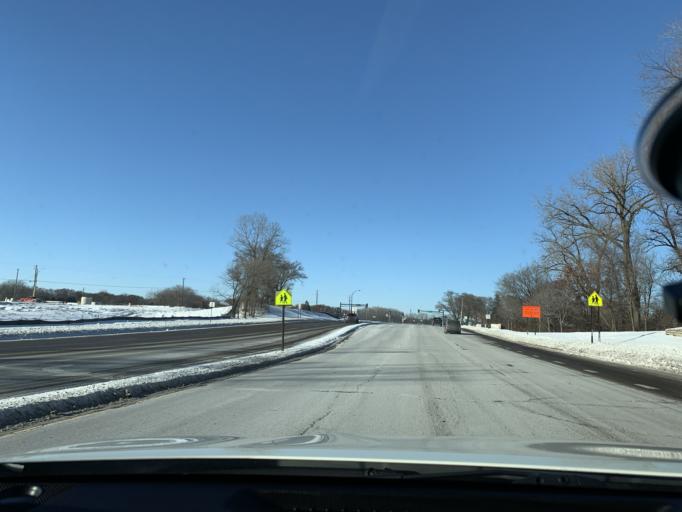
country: US
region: Minnesota
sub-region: Anoka County
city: Coon Rapids
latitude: 45.1510
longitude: -93.2971
